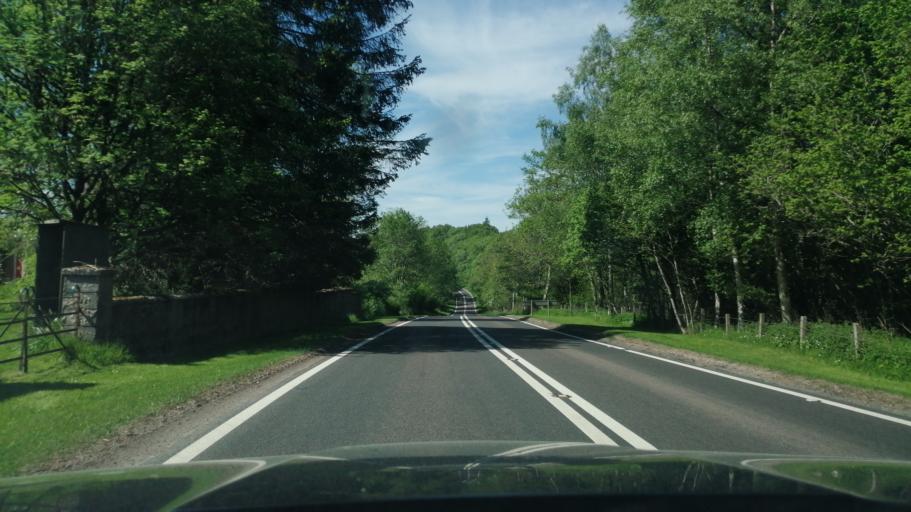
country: GB
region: Scotland
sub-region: Moray
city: Dufftown
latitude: 57.4981
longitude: -3.1411
